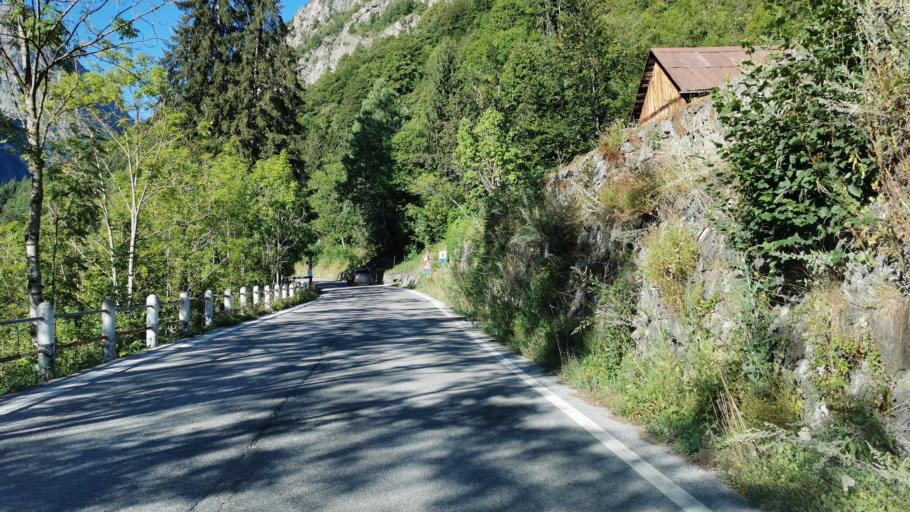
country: IT
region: Piedmont
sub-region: Provincia di Cuneo
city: Demonte
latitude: 44.2424
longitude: 7.3194
